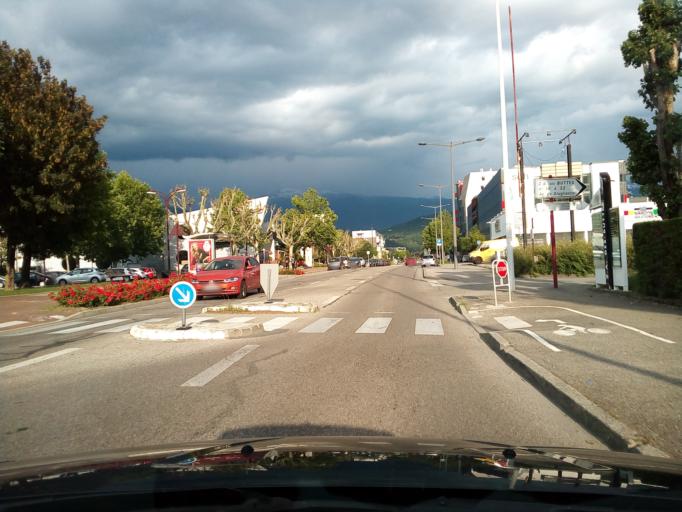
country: FR
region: Rhone-Alpes
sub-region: Departement de l'Isere
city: Echirolles
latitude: 45.1508
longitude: 5.7153
